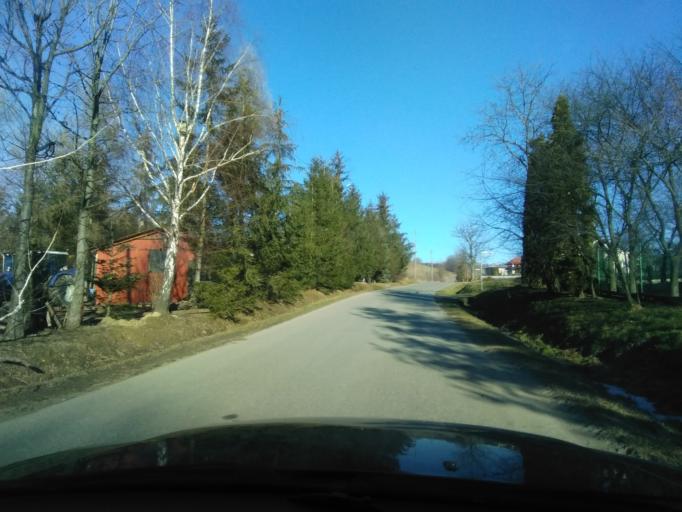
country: PL
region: Subcarpathian Voivodeship
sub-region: Powiat krosnienski
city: Rymanow
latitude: 49.5864
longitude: 21.8889
